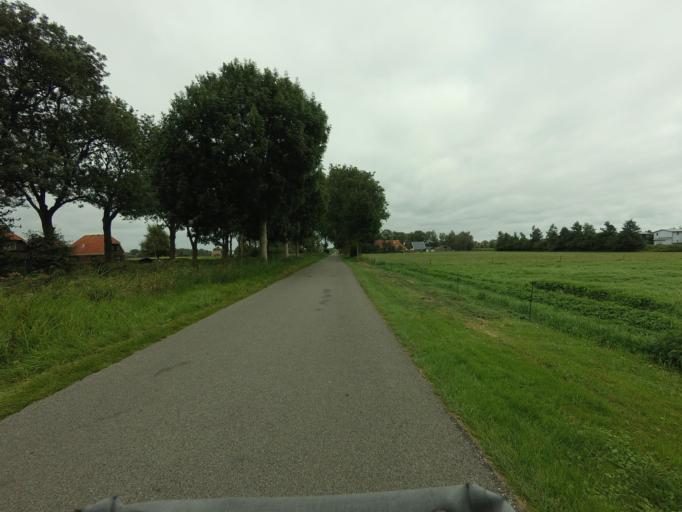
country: NL
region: Overijssel
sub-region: Gemeente Steenwijkerland
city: Giethoorn
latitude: 52.7217
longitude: 6.0661
